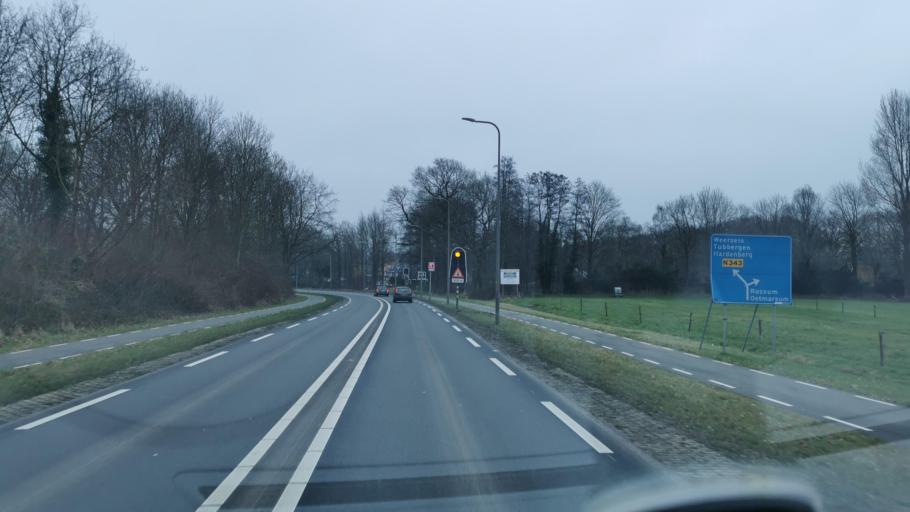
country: NL
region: Overijssel
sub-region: Gemeente Oldenzaal
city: Oldenzaal
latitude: 52.3257
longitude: 6.9341
